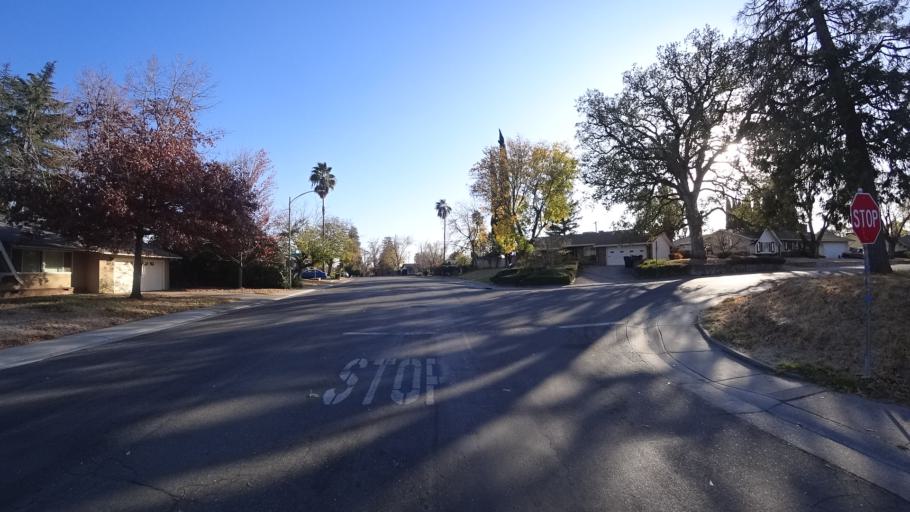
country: US
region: California
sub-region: Sacramento County
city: Citrus Heights
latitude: 38.6947
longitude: -121.2977
